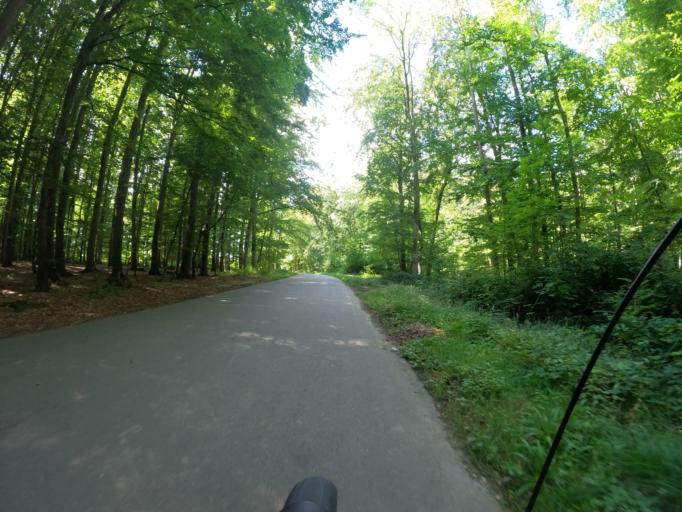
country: DE
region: Schleswig-Holstein
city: Dollerup
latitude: 54.8001
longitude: 9.7163
